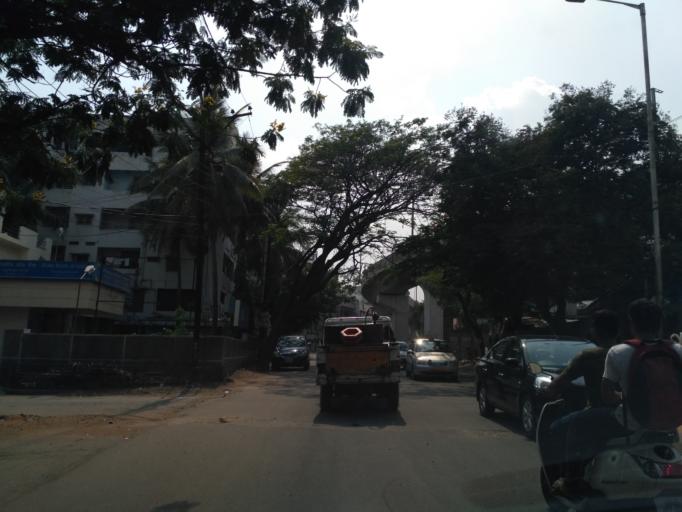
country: IN
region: Telangana
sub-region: Rangareddi
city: Kukatpalli
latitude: 17.4363
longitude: 78.4390
